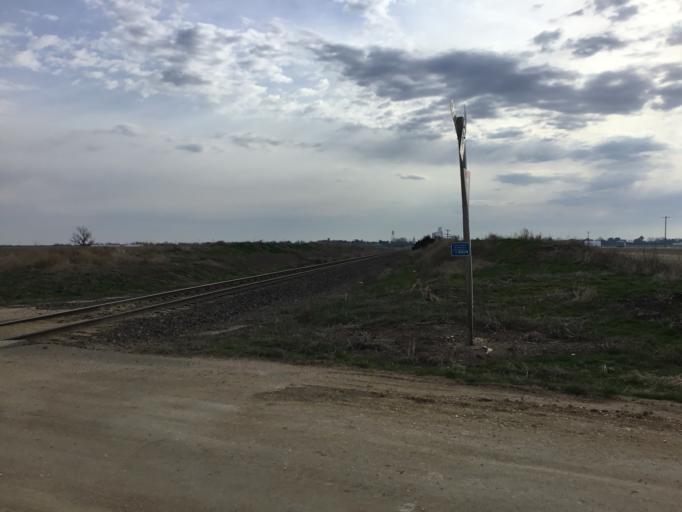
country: US
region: Kansas
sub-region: Ellis County
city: Victoria
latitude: 38.8768
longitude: -99.0399
